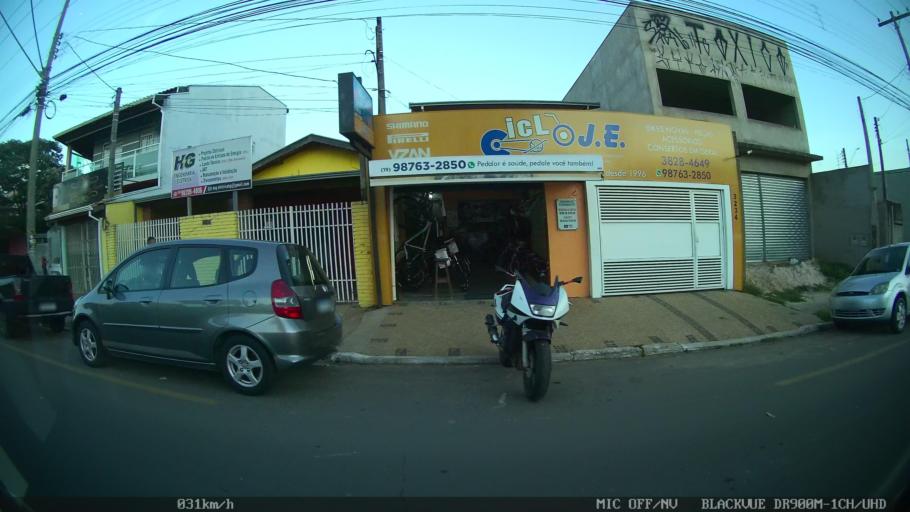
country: BR
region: Sao Paulo
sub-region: Sumare
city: Sumare
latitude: -22.8123
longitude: -47.2338
